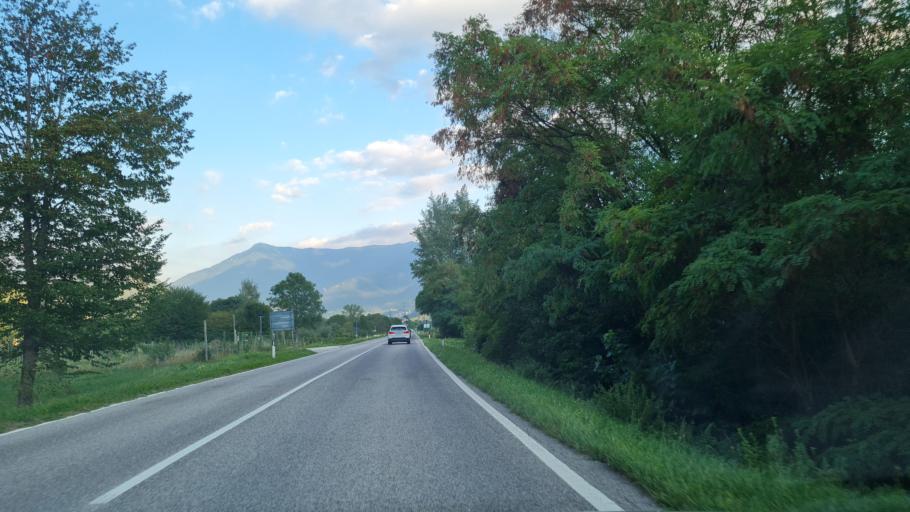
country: IT
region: Veneto
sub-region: Provincia di Belluno
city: Fonzaso
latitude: 46.0202
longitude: 11.7819
